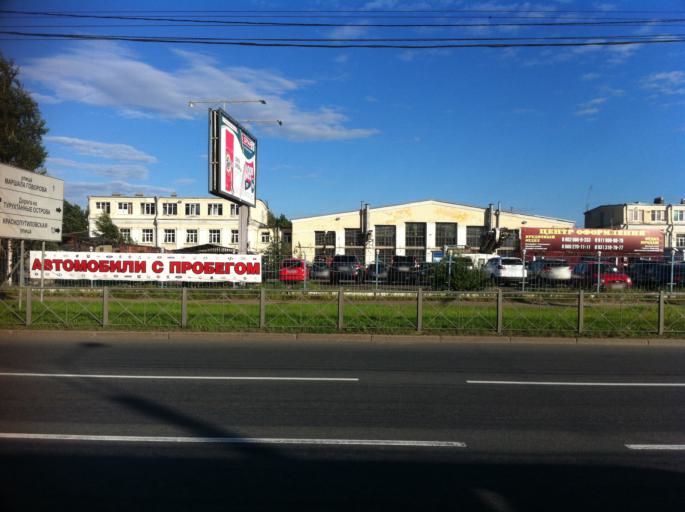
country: RU
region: St.-Petersburg
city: Avtovo
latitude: 59.8685
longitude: 30.2459
